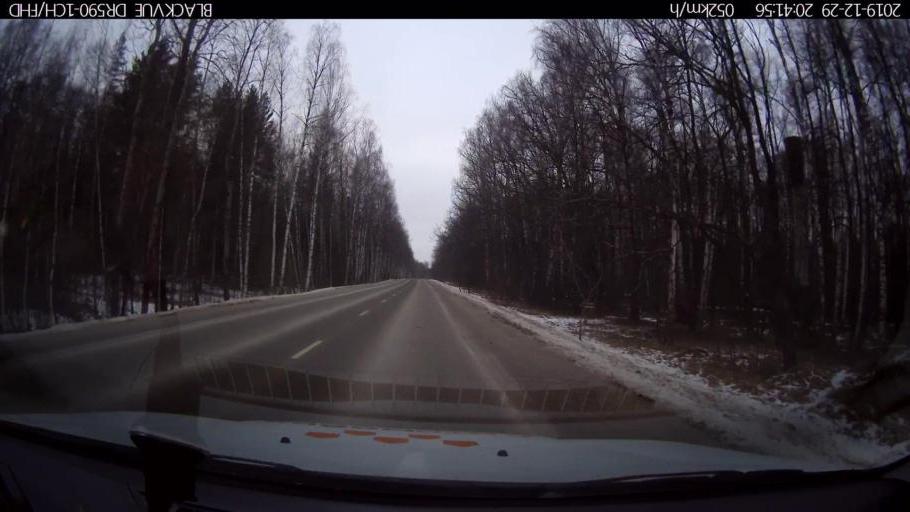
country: RU
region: Nizjnij Novgorod
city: Afonino
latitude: 56.1886
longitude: 44.0338
